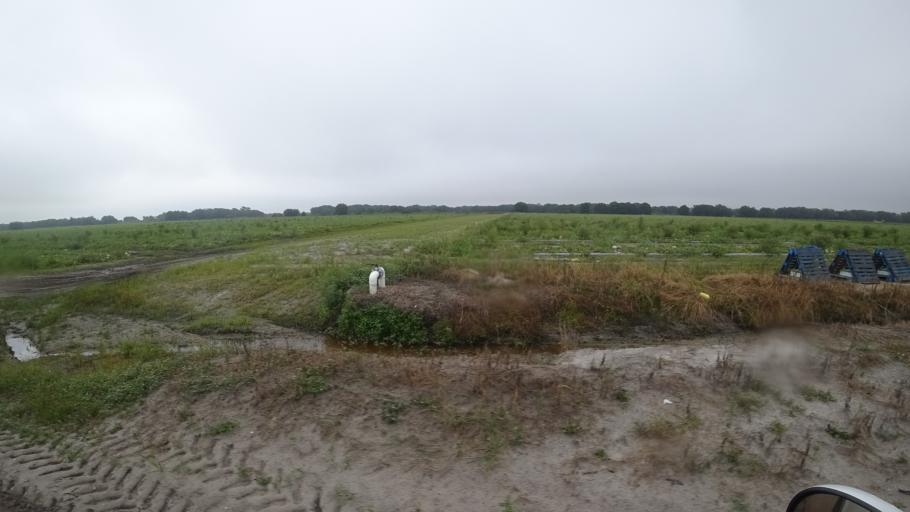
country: US
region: Florida
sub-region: Sarasota County
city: Warm Mineral Springs
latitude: 27.2875
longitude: -82.1583
